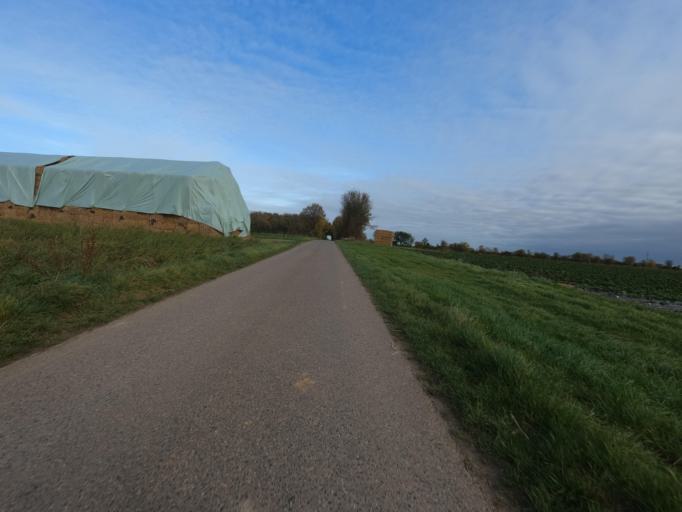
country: DE
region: North Rhine-Westphalia
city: Erkelenz
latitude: 51.0237
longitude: 6.3120
